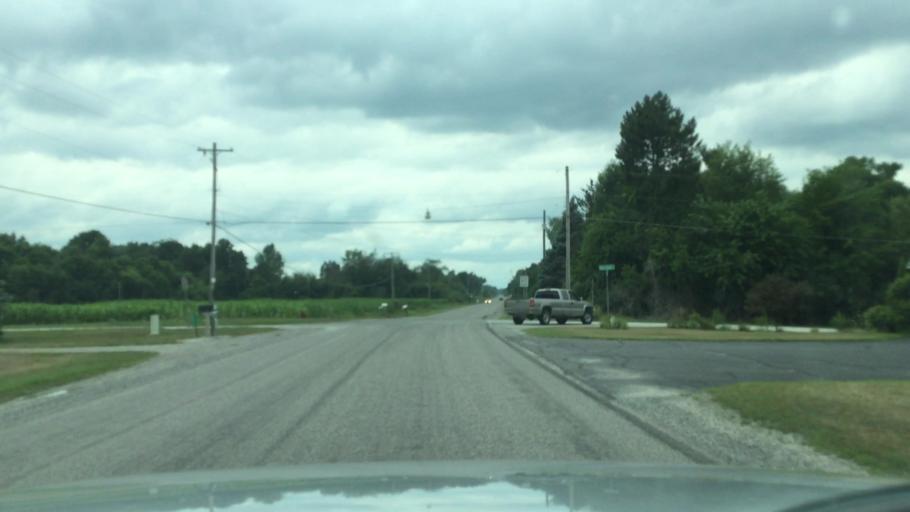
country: US
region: Michigan
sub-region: Saginaw County
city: Burt
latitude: 43.2501
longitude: -83.8537
